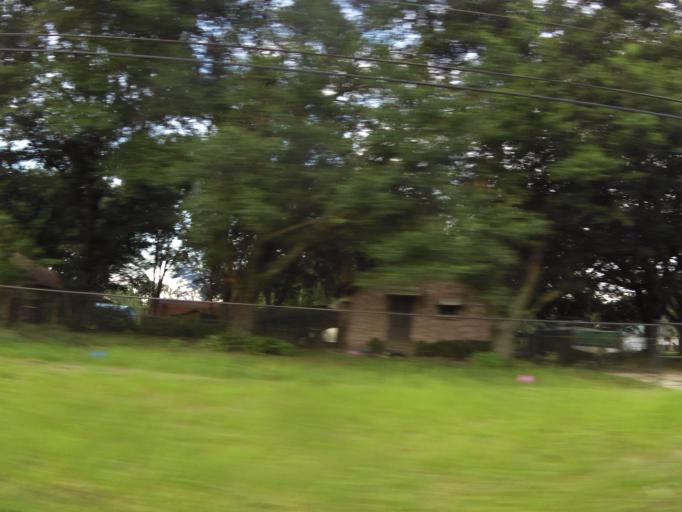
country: US
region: Florida
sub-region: Nassau County
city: Nassau Village-Ratliff
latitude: 30.3607
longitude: -81.8069
